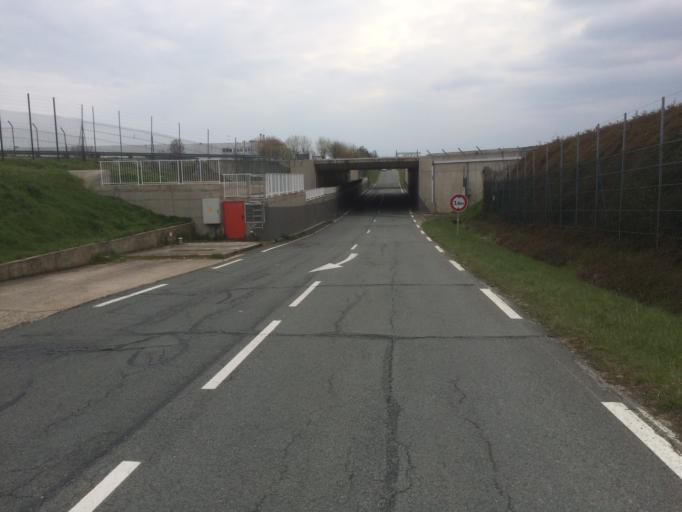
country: FR
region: Ile-de-France
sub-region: Departement de l'Essonne
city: Paray-Vieille-Poste
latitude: 48.7251
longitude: 2.3466
